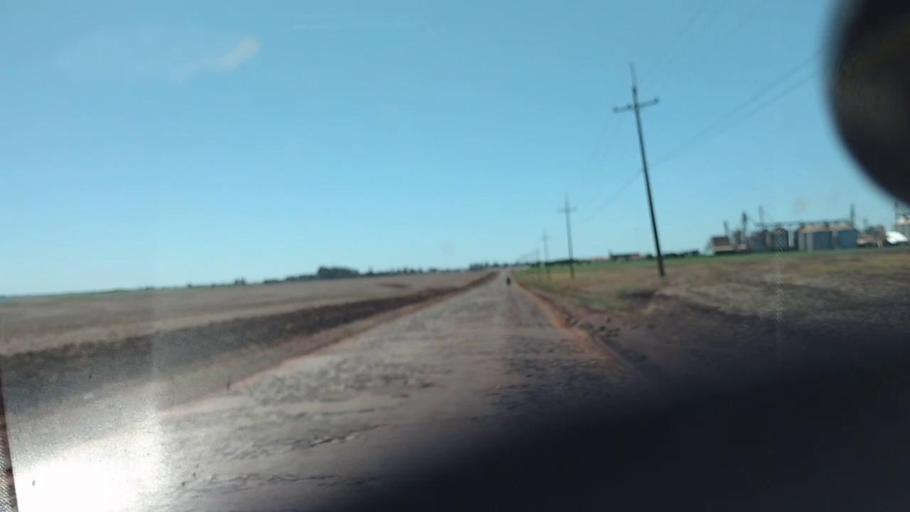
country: PY
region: Alto Parana
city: Naranjal
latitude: -25.9746
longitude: -55.1564
